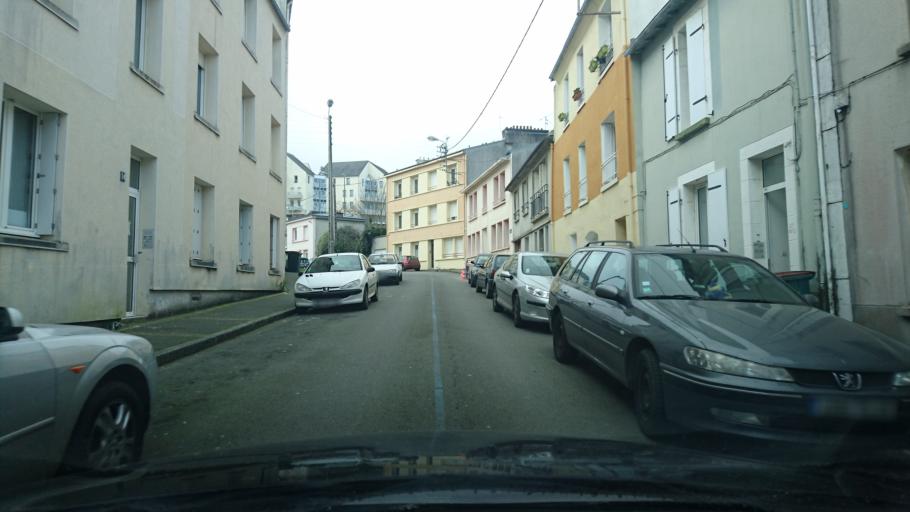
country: FR
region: Brittany
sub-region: Departement du Finistere
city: Brest
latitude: 48.3895
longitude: -4.5020
